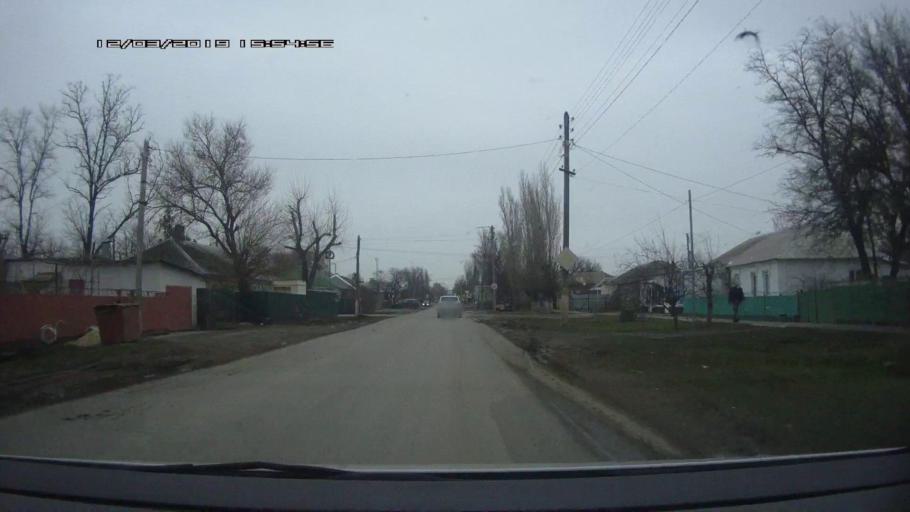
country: RU
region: Rostov
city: Novobataysk
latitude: 46.8937
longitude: 39.7787
